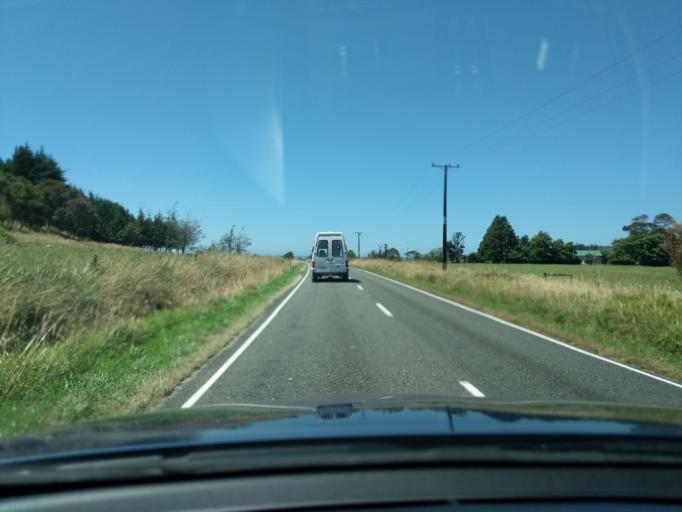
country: NZ
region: Tasman
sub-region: Tasman District
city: Takaka
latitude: -40.6911
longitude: 172.6438
